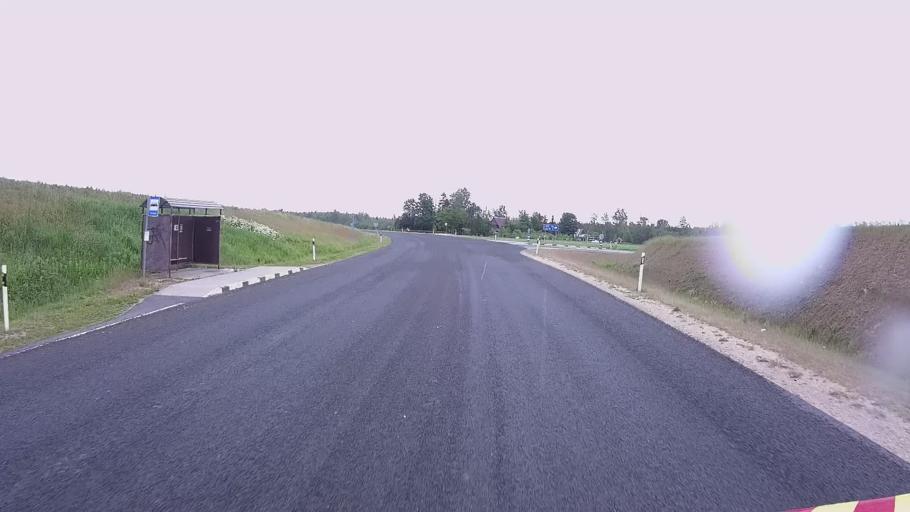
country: EE
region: Jogevamaa
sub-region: Poltsamaa linn
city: Poltsamaa
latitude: 58.5396
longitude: 25.9558
